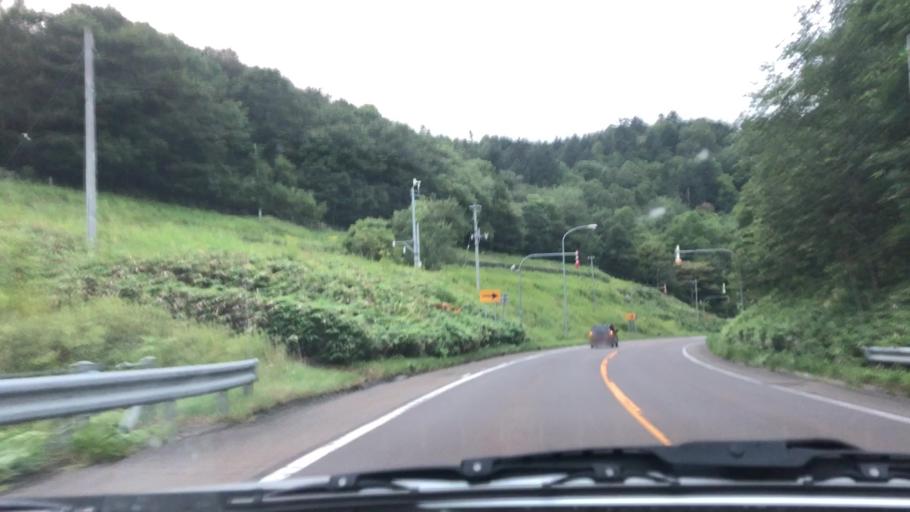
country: JP
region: Hokkaido
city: Iwamizawa
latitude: 42.9195
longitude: 142.1167
